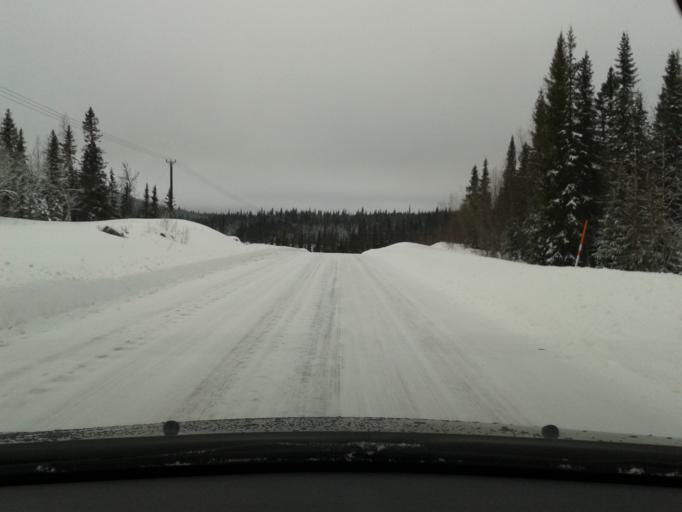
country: SE
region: Vaesterbotten
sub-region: Vilhelmina Kommun
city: Sjoberg
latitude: 65.1864
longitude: 15.9404
